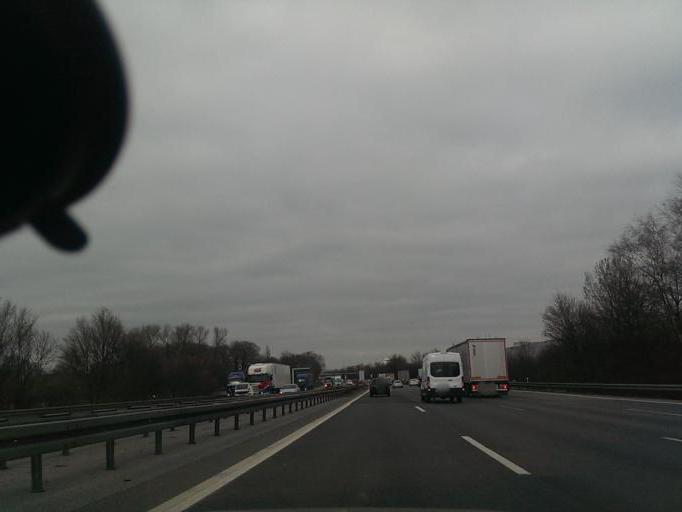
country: DE
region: North Rhine-Westphalia
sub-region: Regierungsbezirk Detmold
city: Guetersloh
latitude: 51.8837
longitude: 8.4347
